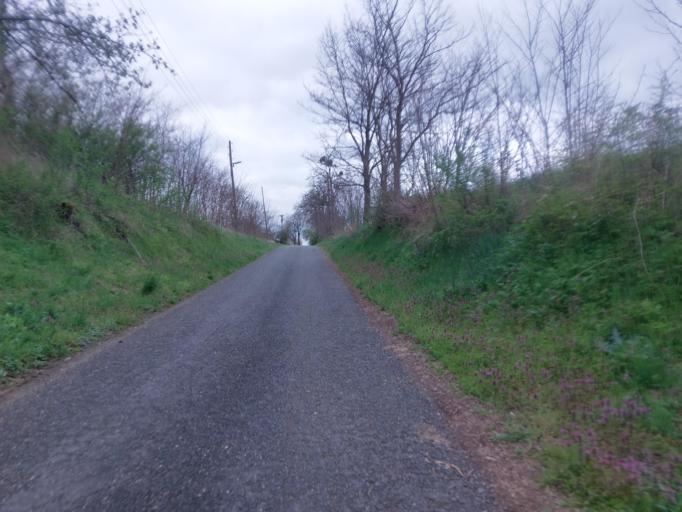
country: HU
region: Veszprem
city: Devecser
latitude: 47.1321
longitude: 17.4004
